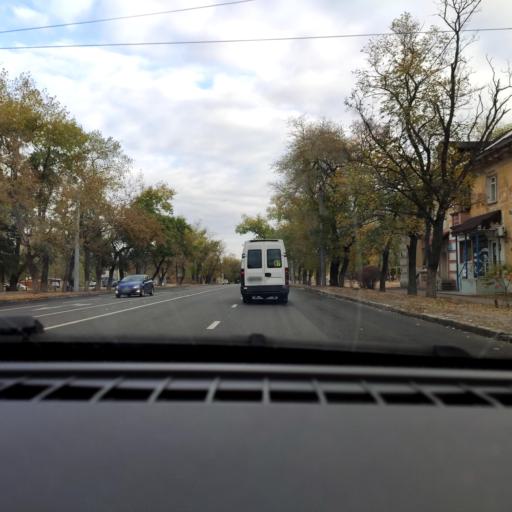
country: RU
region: Voronezj
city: Maslovka
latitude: 51.6165
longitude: 39.2486
